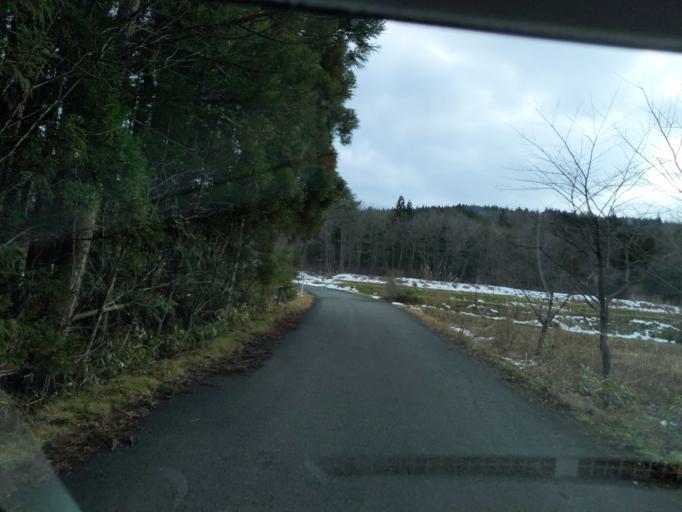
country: JP
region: Iwate
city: Ichinoseki
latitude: 38.9965
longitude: 140.9982
